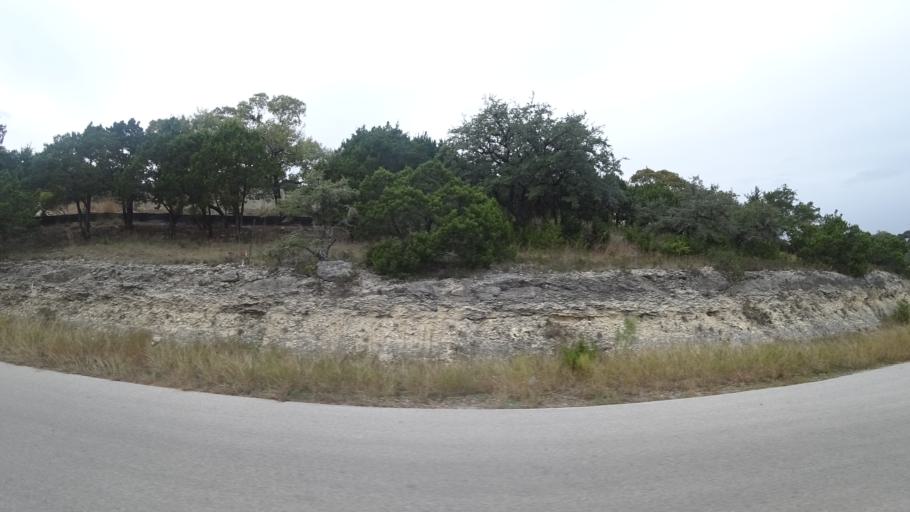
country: US
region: Texas
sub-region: Travis County
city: Hudson Bend
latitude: 30.3700
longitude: -97.9187
